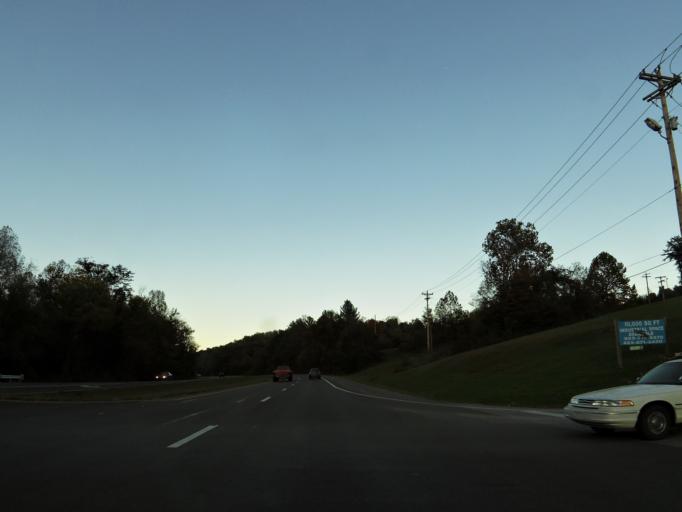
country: US
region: Tennessee
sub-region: Campbell County
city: Caryville
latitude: 36.3114
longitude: -84.2082
